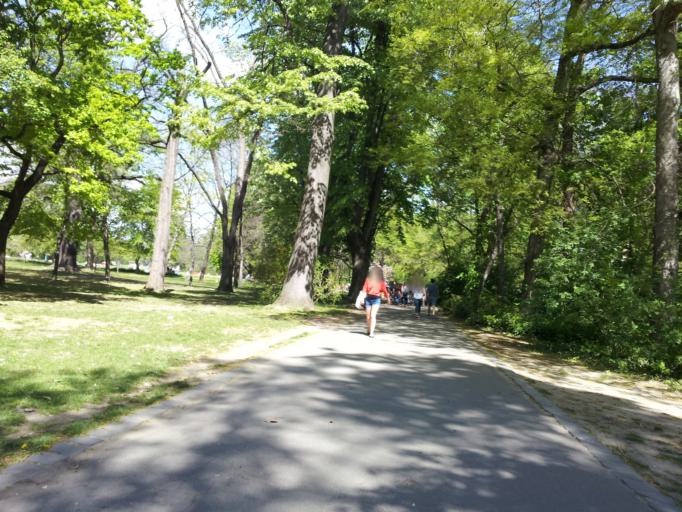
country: HU
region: Budapest
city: Budapest II. keruelet
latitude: 47.5227
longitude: 19.0478
